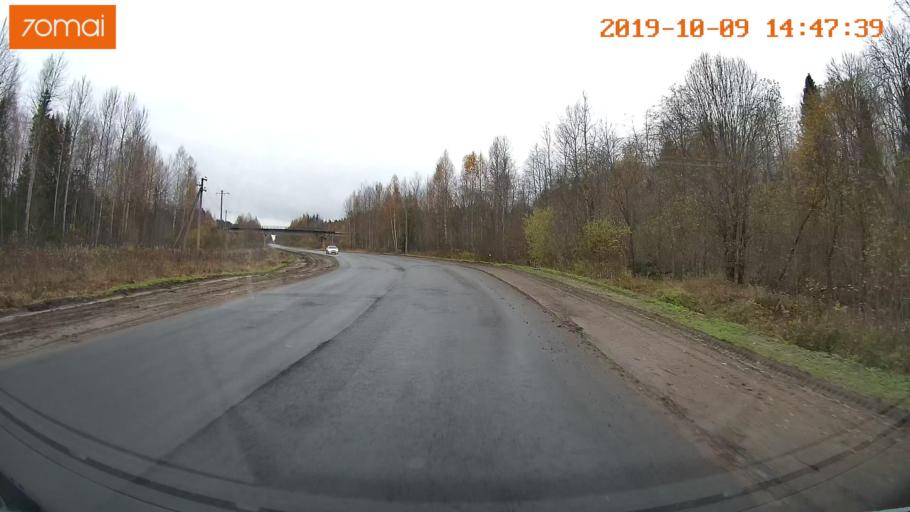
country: RU
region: Kostroma
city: Buy
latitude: 58.4153
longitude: 41.5718
